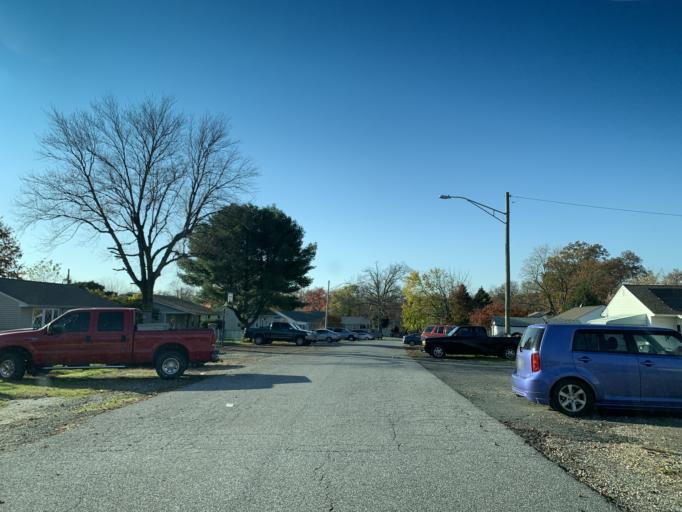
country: US
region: Maryland
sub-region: Baltimore County
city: Middle River
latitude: 39.3403
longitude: -76.4563
